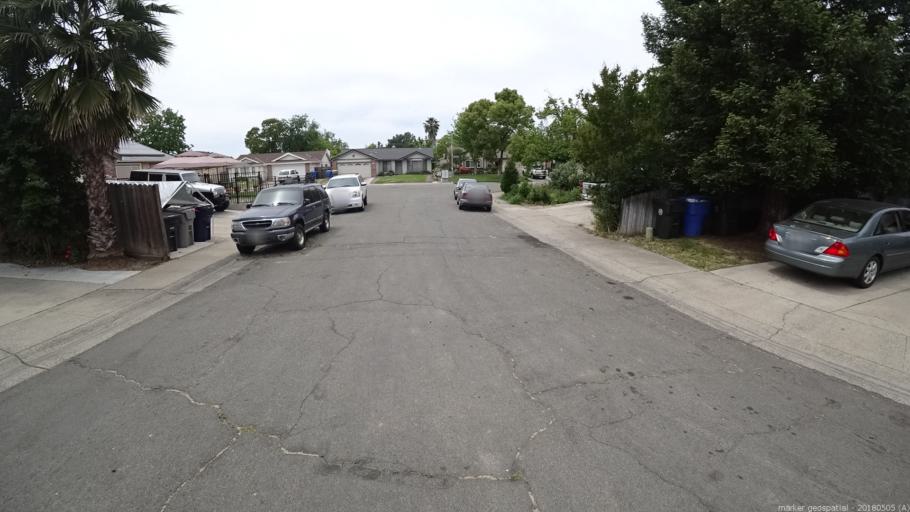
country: US
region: California
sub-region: Sacramento County
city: Rio Linda
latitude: 38.6521
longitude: -121.4620
